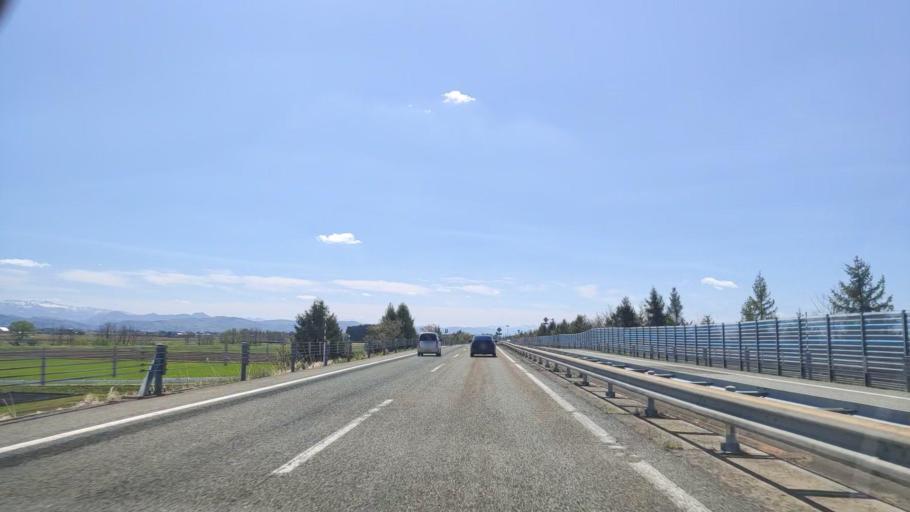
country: JP
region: Akita
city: Omagari
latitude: 39.3704
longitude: 140.4852
